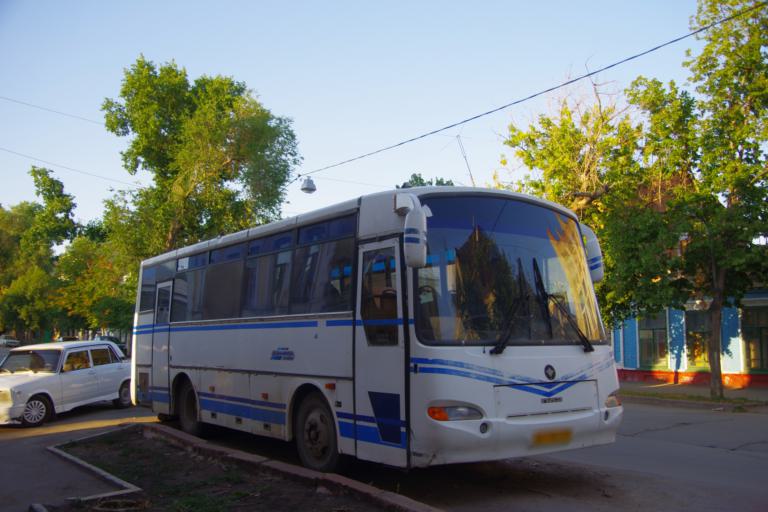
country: RU
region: Samara
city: Samara
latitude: 53.1892
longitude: 50.0981
